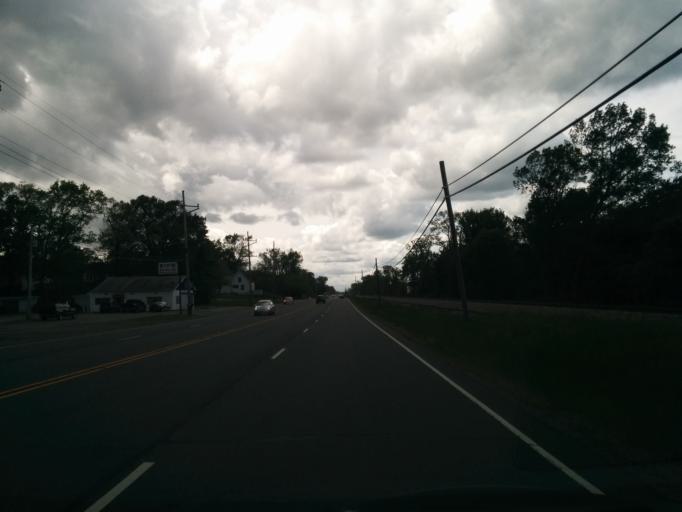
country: US
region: Indiana
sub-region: LaPorte County
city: Long Beach
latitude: 41.7377
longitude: -86.8460
